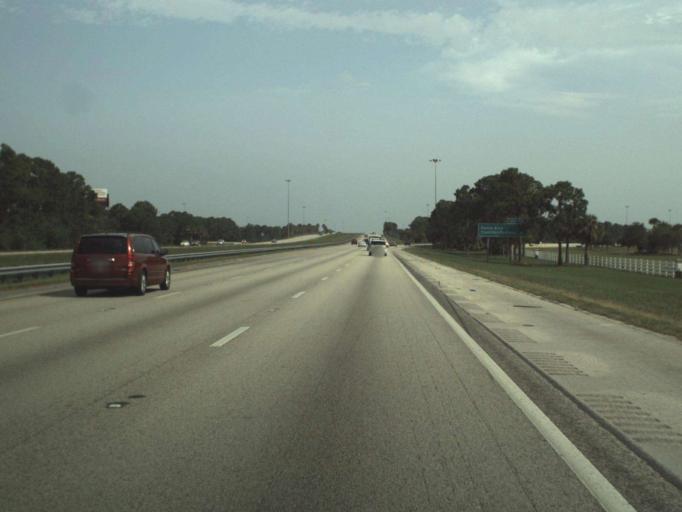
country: US
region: Florida
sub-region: Saint Lucie County
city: Port Saint Lucie
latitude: 27.2722
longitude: -80.4253
